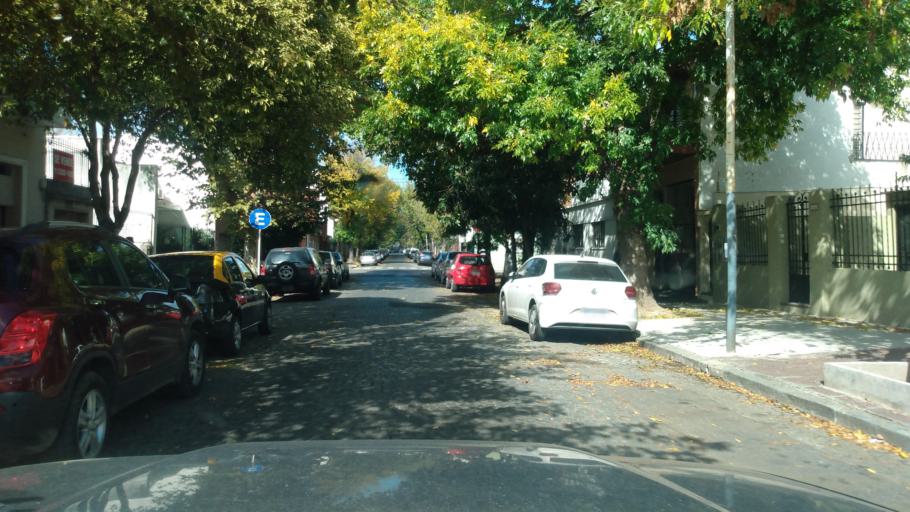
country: AR
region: Buenos Aires
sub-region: Partido de General San Martin
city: General San Martin
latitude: -34.5691
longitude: -58.4956
